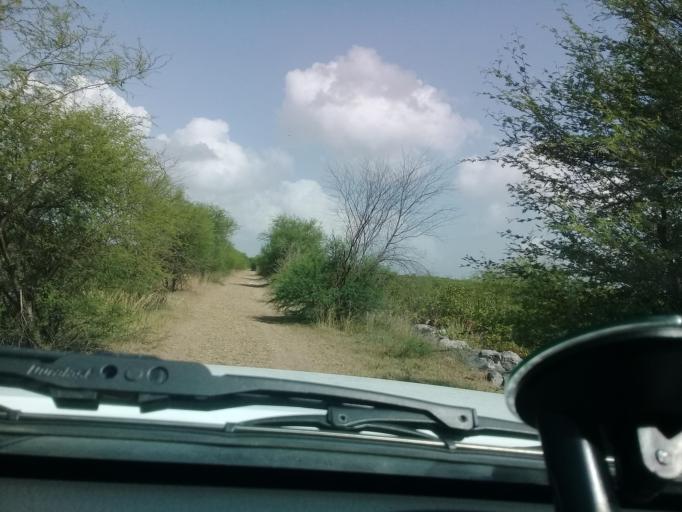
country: MX
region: Veracruz
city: Moralillo
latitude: 22.2294
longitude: -97.8999
